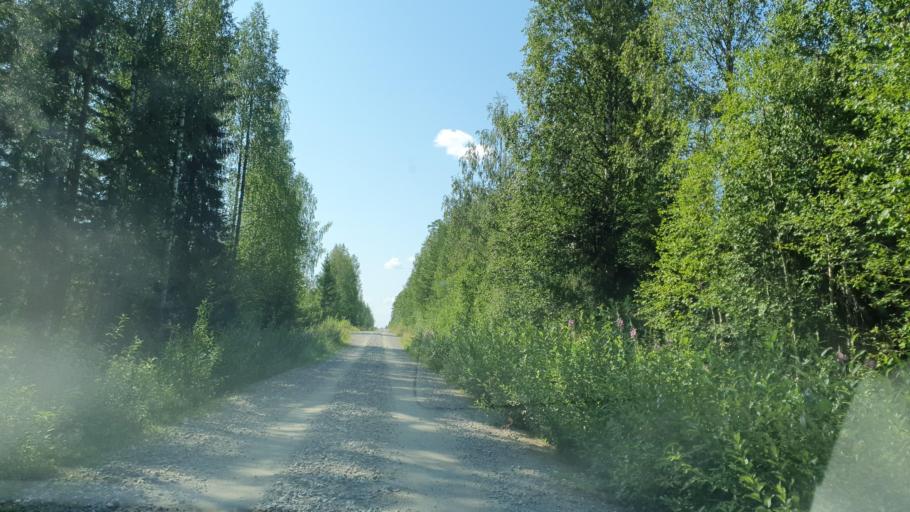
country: FI
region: Kainuu
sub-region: Kehys-Kainuu
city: Kuhmo
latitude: 64.0101
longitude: 29.5806
